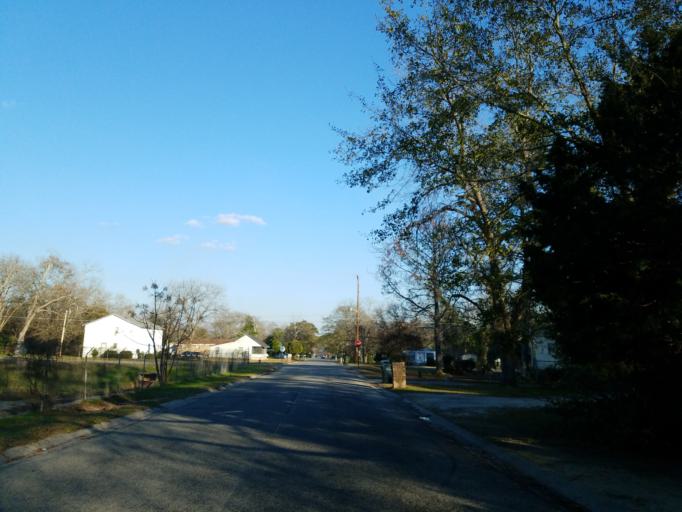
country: US
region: Georgia
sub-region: Crisp County
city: Cordele
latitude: 31.9602
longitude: -83.7871
